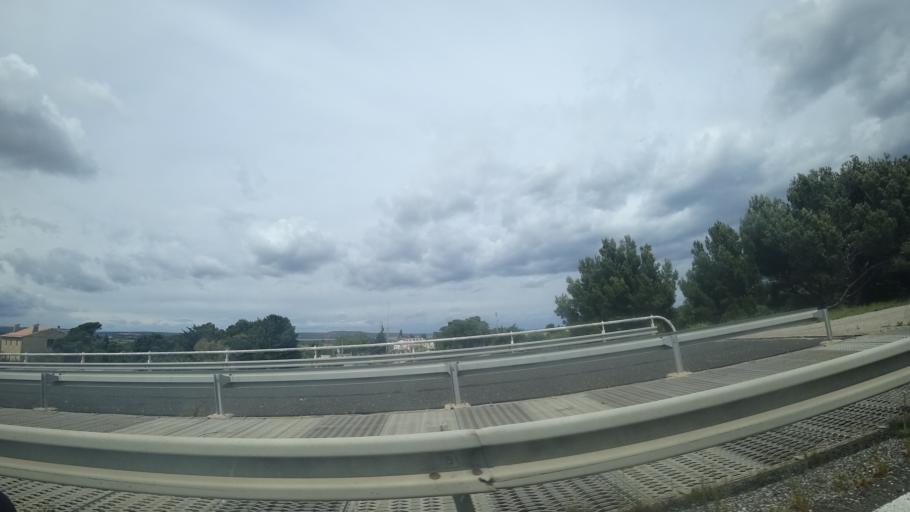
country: FR
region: Languedoc-Roussillon
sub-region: Departement de l'Aude
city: Leucate
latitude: 42.9312
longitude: 3.0123
